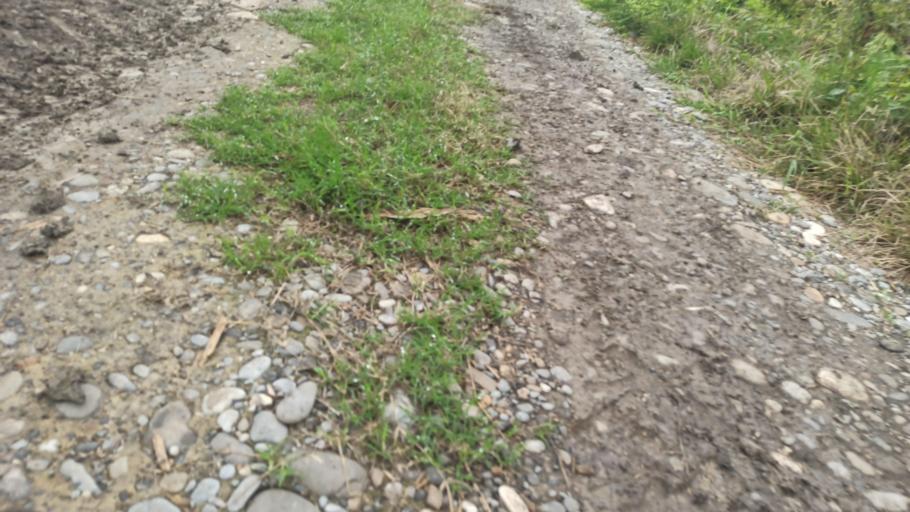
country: MX
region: Puebla
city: Espinal
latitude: 20.2983
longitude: -97.4045
